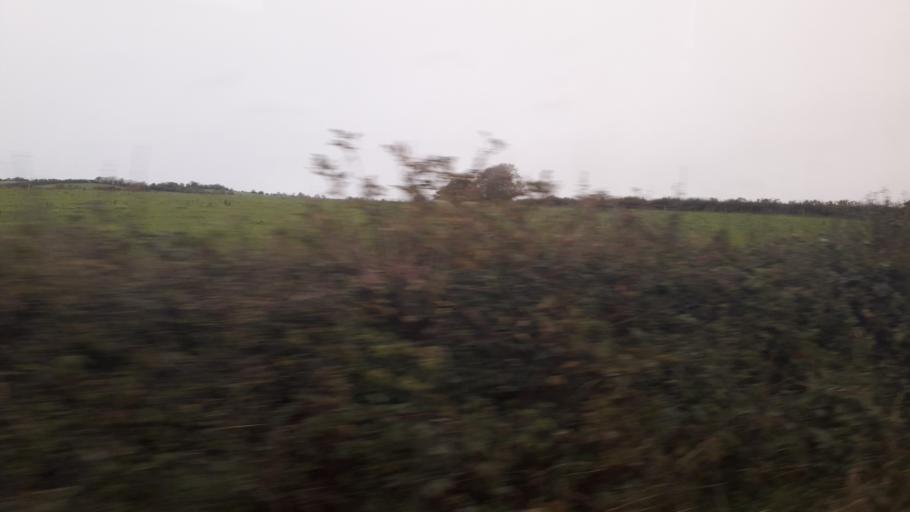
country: IE
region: Leinster
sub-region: Uibh Fhaili
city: Birr
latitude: 52.9754
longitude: -7.9885
